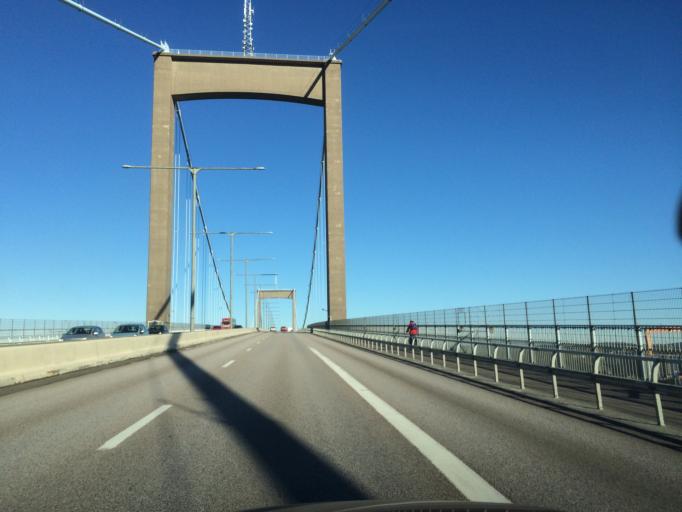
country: SE
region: Vaestra Goetaland
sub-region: Goteborg
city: Majorna
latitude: 57.6879
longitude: 11.9036
